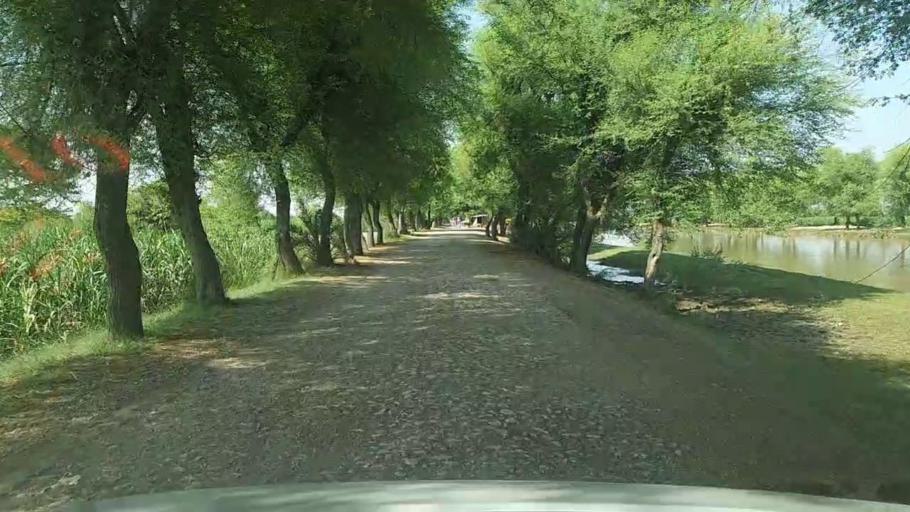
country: PK
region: Sindh
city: Mirpur Mathelo
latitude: 28.1201
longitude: 69.5976
